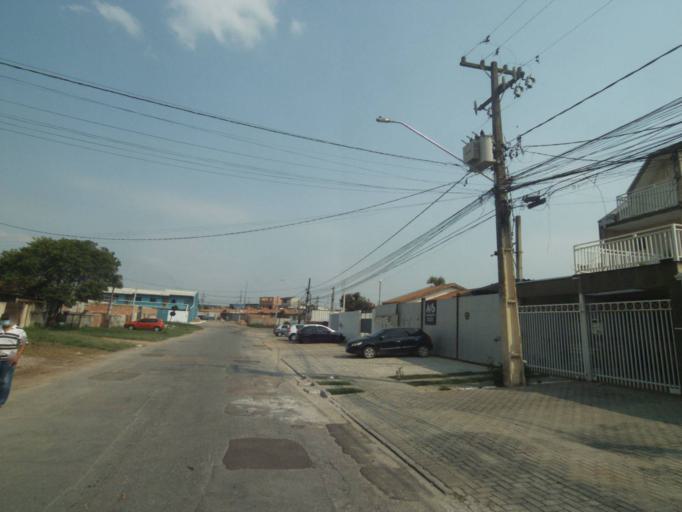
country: BR
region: Parana
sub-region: Sao Jose Dos Pinhais
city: Sao Jose dos Pinhais
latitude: -25.5286
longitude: -49.2312
